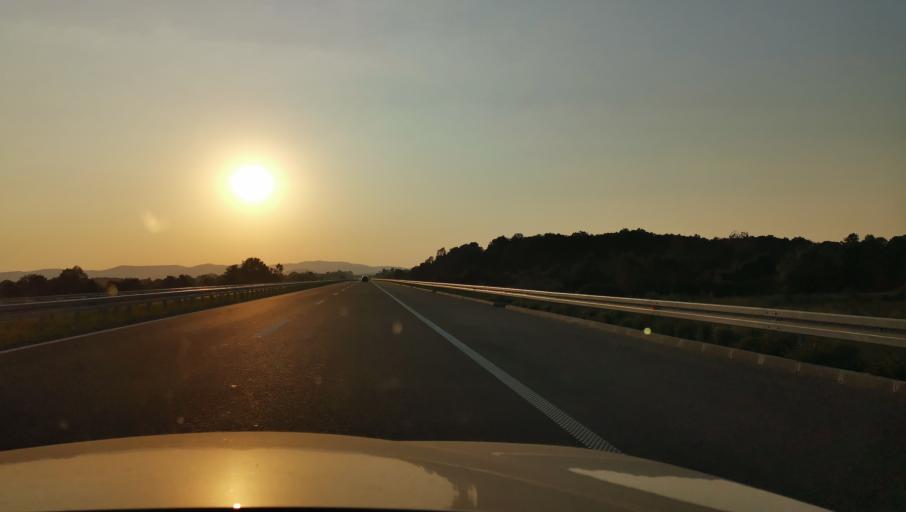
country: RS
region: Central Serbia
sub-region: Kolubarski Okrug
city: Lajkovac
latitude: 44.3486
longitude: 20.1666
